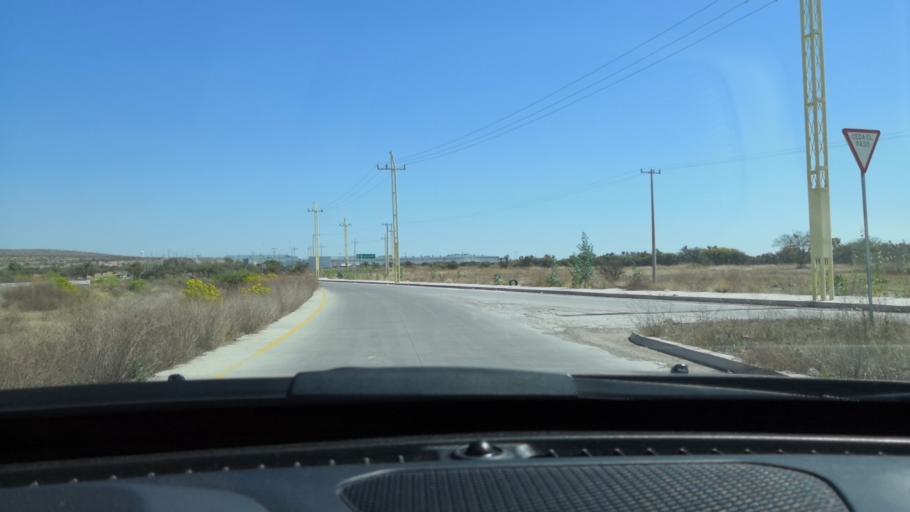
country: MX
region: Guanajuato
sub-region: Leon
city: Centro Familiar la Soledad
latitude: 21.1005
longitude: -101.7762
